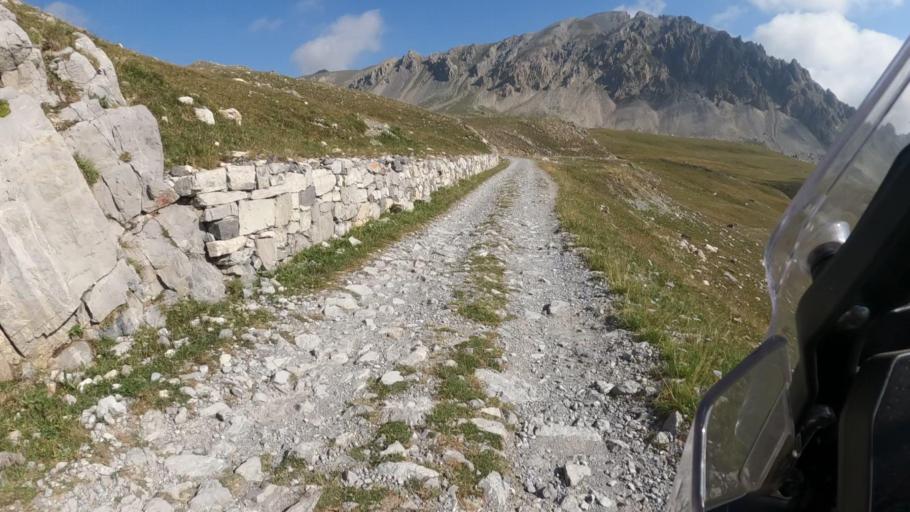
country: IT
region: Piedmont
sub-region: Provincia di Cuneo
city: Bersezio
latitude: 44.4026
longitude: 7.0158
